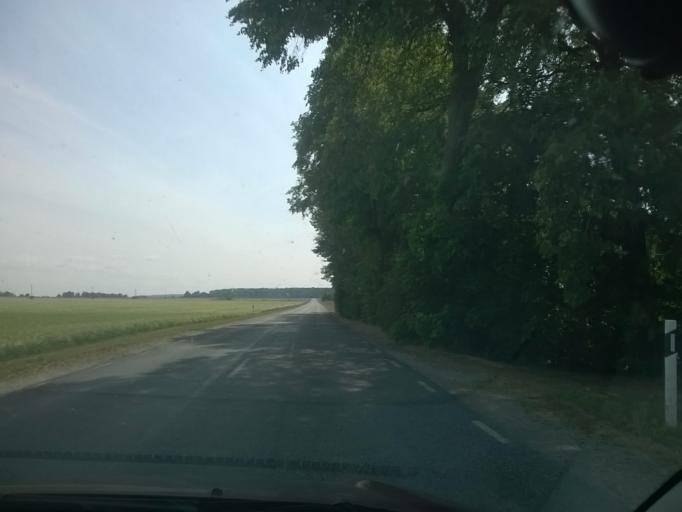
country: EE
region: Tartu
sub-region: Puhja vald
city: Puhja
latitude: 58.2691
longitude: 26.1759
